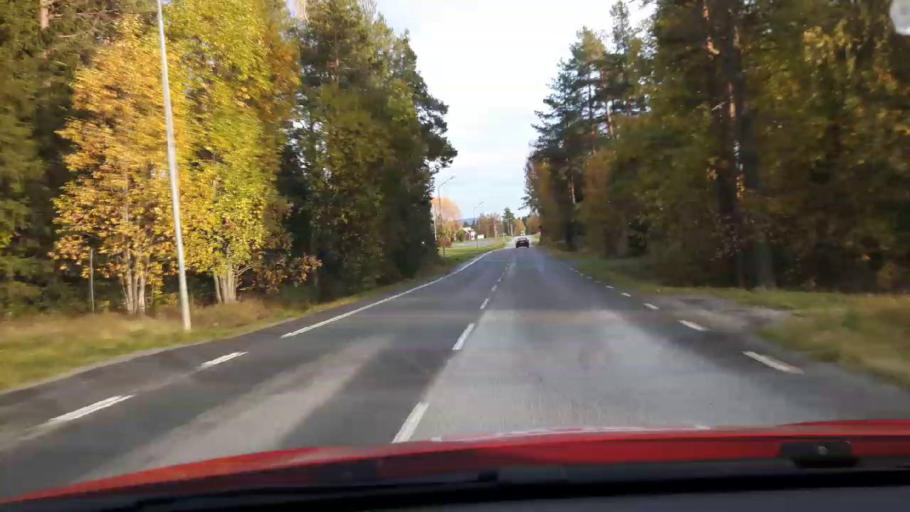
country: SE
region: Jaemtland
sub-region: Krokoms Kommun
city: Krokom
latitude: 63.3421
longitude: 14.5770
